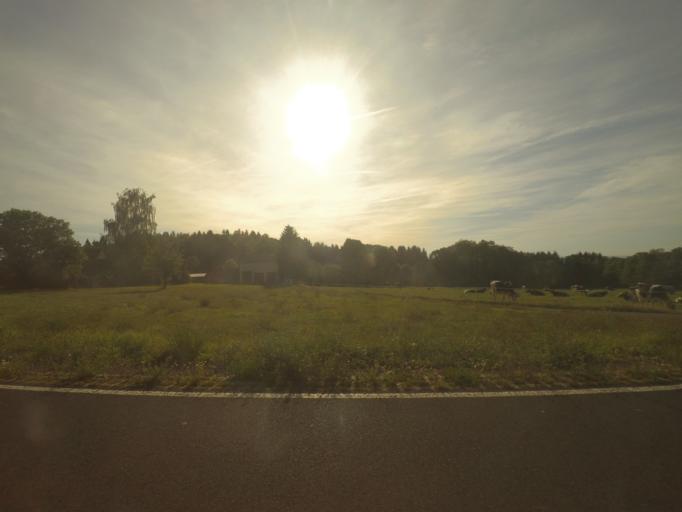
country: DE
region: Hesse
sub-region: Regierungsbezirk Kassel
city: Poppenhausen
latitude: 50.5257
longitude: 9.8673
